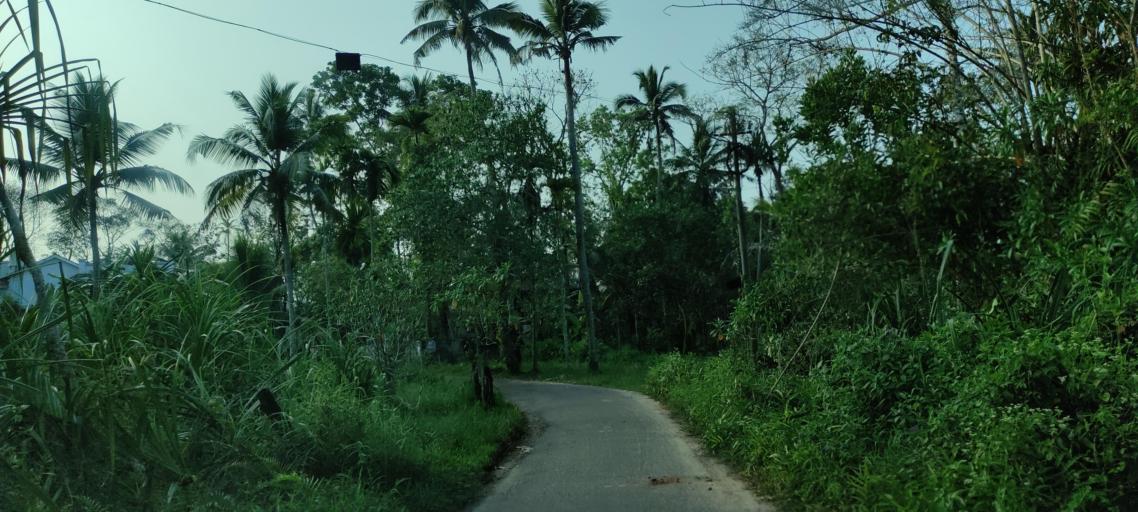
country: IN
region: Kerala
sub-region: Alappuzha
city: Shertallai
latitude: 9.6692
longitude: 76.3549
